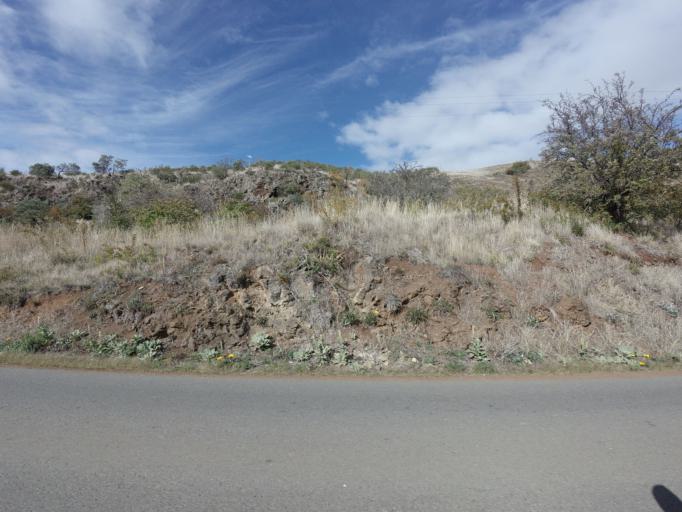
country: AU
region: Tasmania
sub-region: Derwent Valley
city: New Norfolk
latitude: -42.7041
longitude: 146.9155
